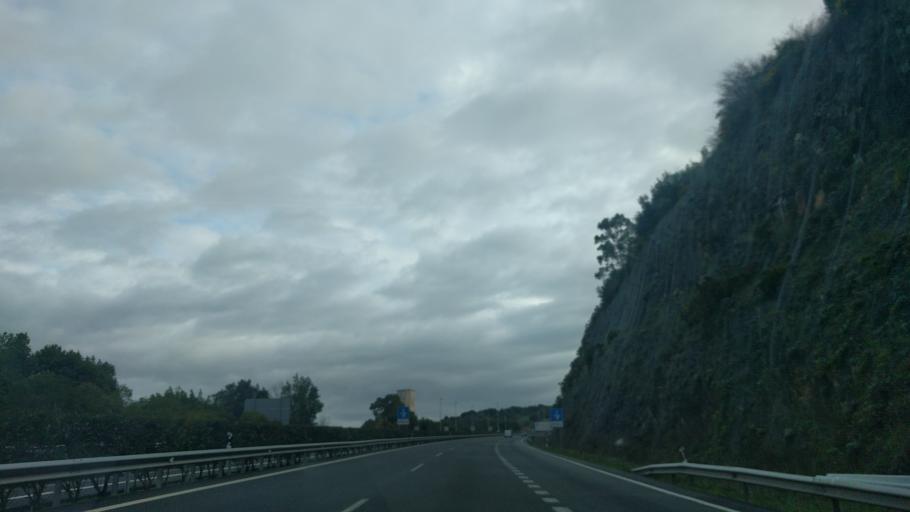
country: ES
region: Cantabria
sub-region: Provincia de Cantabria
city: Laredo
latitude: 43.4034
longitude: -3.4190
